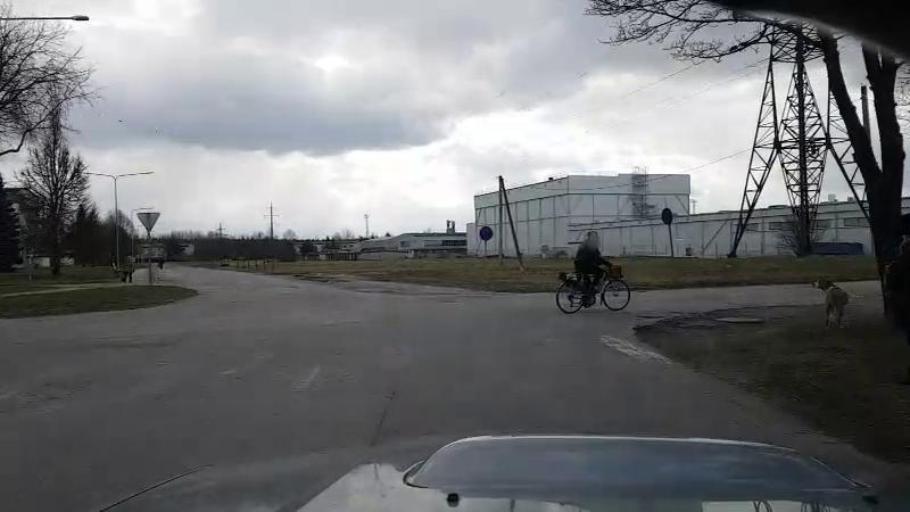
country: EE
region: Jaervamaa
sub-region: Paide linn
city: Paide
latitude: 58.8824
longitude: 25.5639
